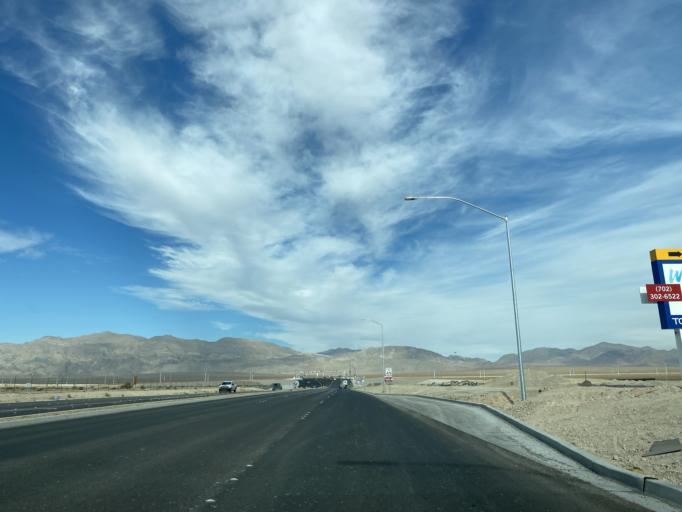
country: US
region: Nevada
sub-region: Clark County
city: Nellis Air Force Base
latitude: 36.2838
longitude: -115.1168
